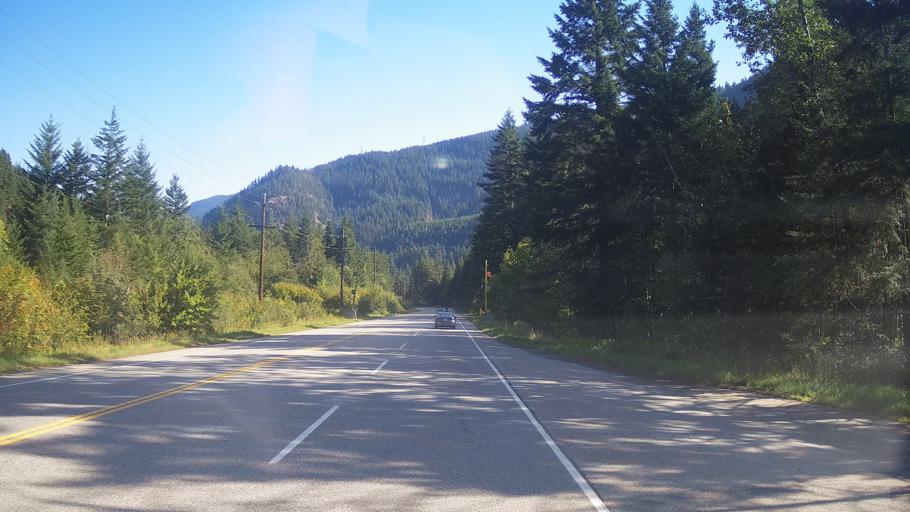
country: CA
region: British Columbia
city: Hope
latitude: 49.6497
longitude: -121.4080
